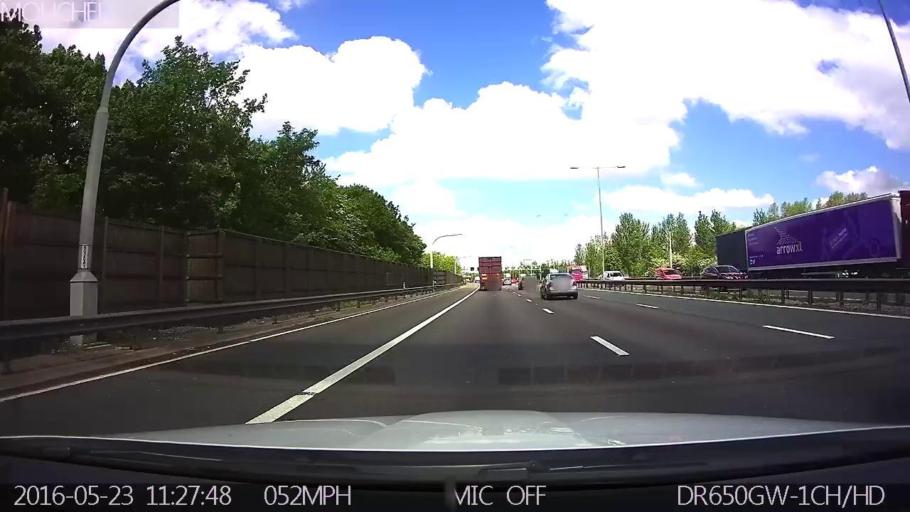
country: GB
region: England
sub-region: Walsall
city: Bloxwich
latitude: 52.6179
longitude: -2.0313
